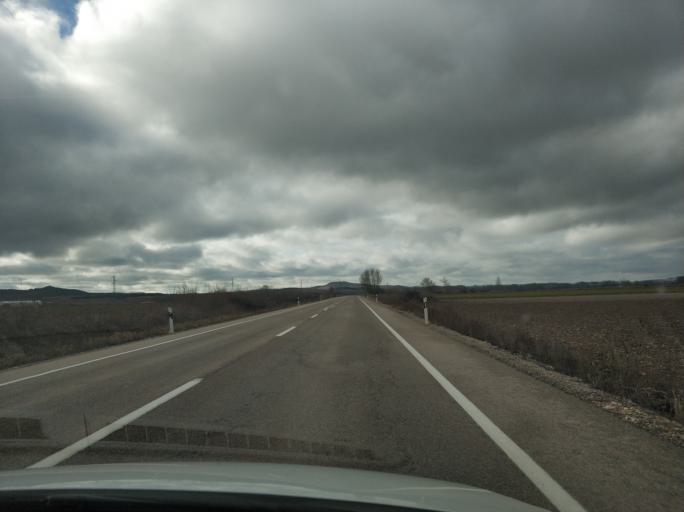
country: ES
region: Castille and Leon
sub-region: Provincia de Soria
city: San Esteban de Gormaz
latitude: 41.5679
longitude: -3.2271
